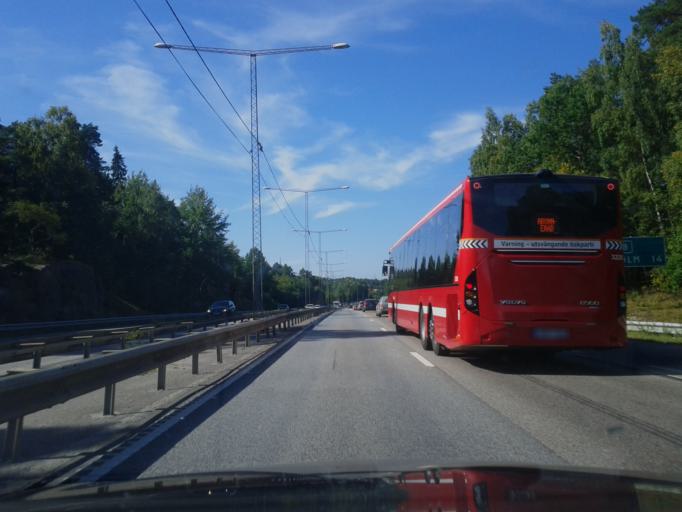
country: SE
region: Stockholm
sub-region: Taby Kommun
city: Taby
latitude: 59.4410
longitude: 18.0899
